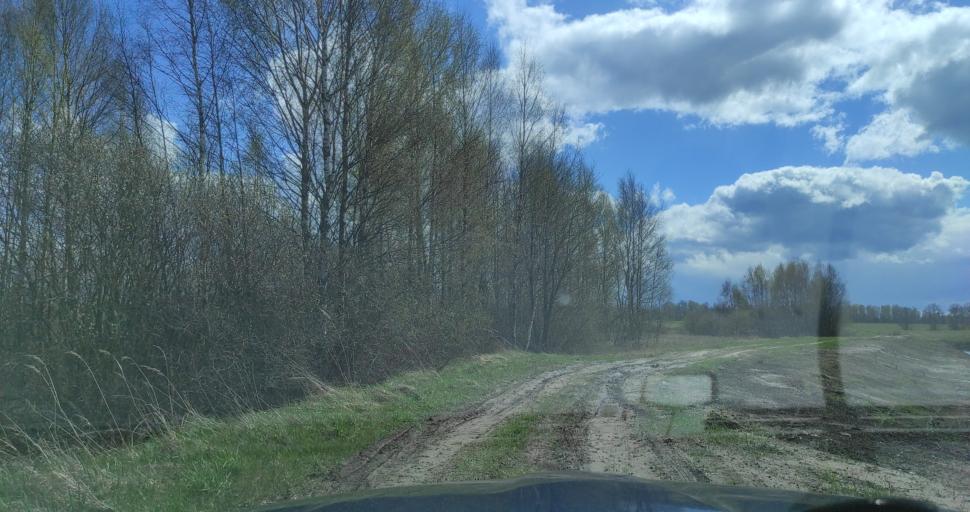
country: LV
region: Kuldigas Rajons
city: Kuldiga
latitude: 56.8737
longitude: 21.7897
